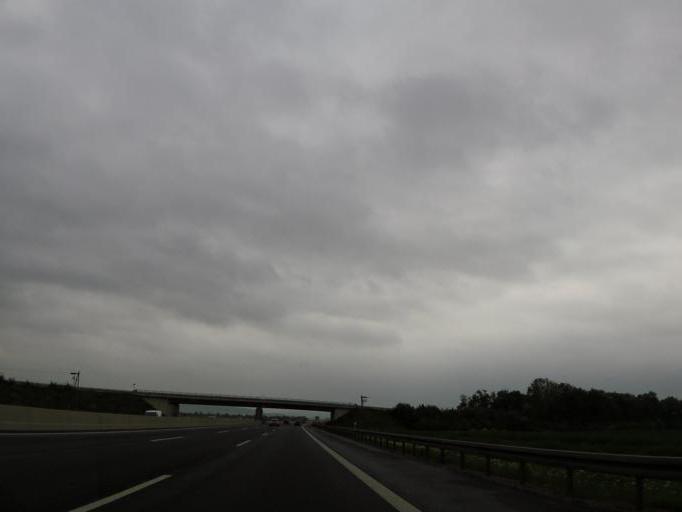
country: DE
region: Lower Saxony
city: Bockenem
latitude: 52.0192
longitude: 10.1678
